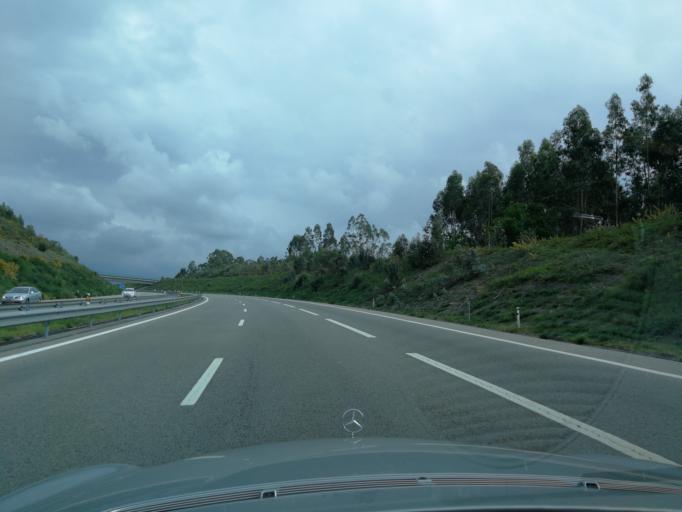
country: PT
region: Porto
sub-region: Vila do Conde
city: Arvore
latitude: 41.3805
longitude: -8.6618
